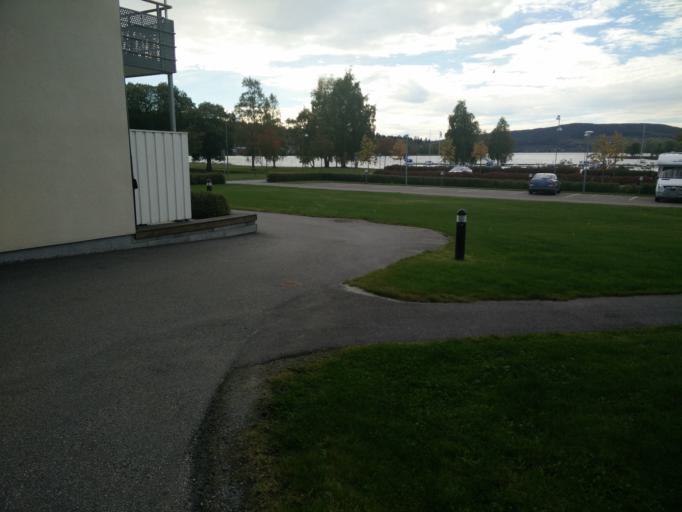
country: SE
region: Vaesternorrland
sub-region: Haernoesands Kommun
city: Haernoesand
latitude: 62.6281
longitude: 17.9444
